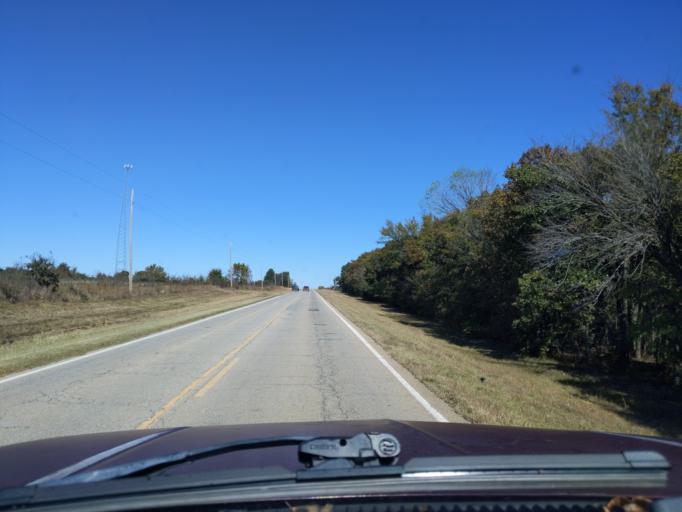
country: US
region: Oklahoma
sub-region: Creek County
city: Bristow
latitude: 35.7162
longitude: -96.3872
